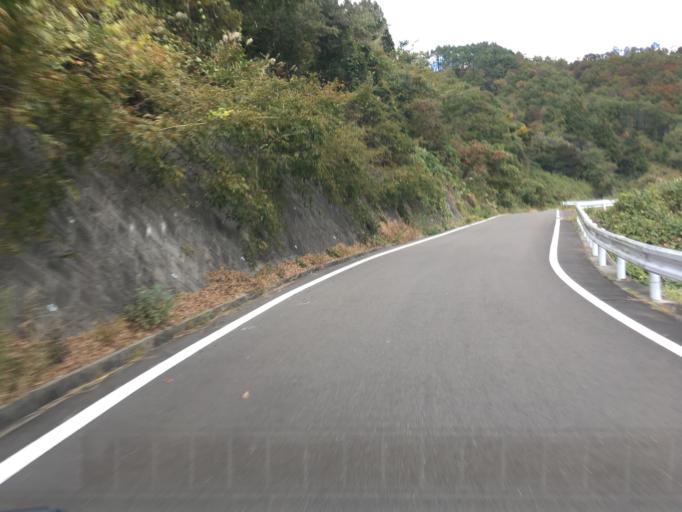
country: JP
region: Miyagi
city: Marumori
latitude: 37.7961
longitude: 140.7534
